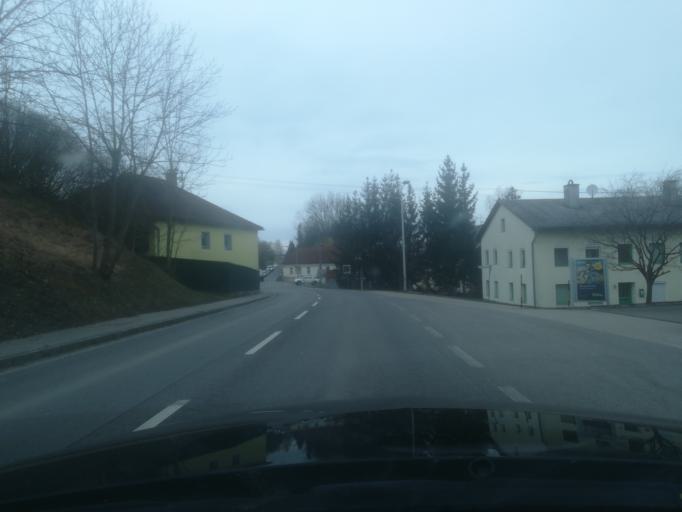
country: AT
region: Upper Austria
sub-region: Wels-Land
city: Gunskirchen
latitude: 48.0864
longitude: 13.9480
